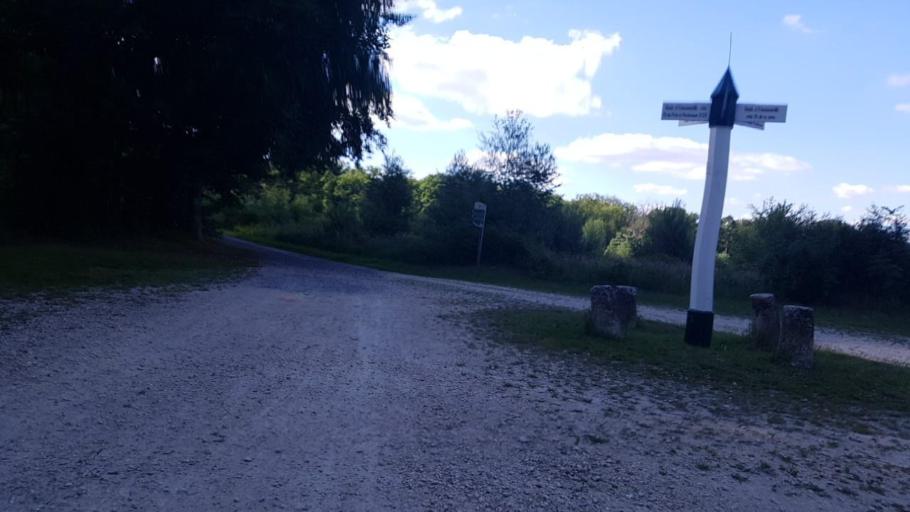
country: FR
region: Picardie
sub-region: Departement de l'Oise
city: Ver-sur-Launette
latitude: 49.1395
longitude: 2.6562
